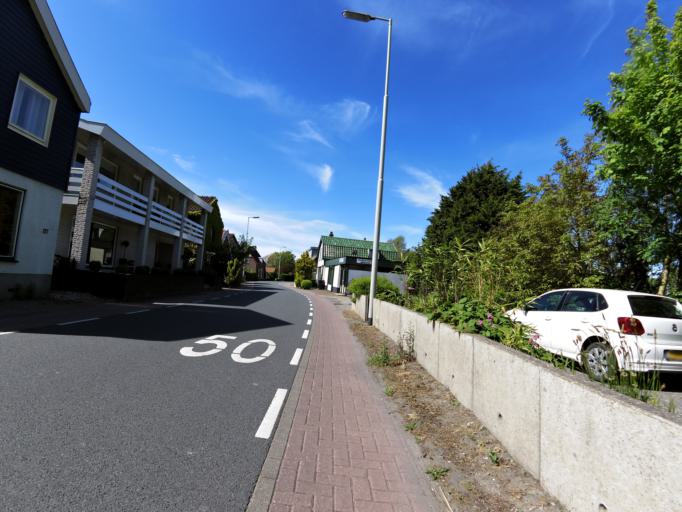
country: NL
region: South Holland
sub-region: Gemeente Hellevoetsluis
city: Nieuwenhoorn
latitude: 51.8500
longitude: 4.1392
